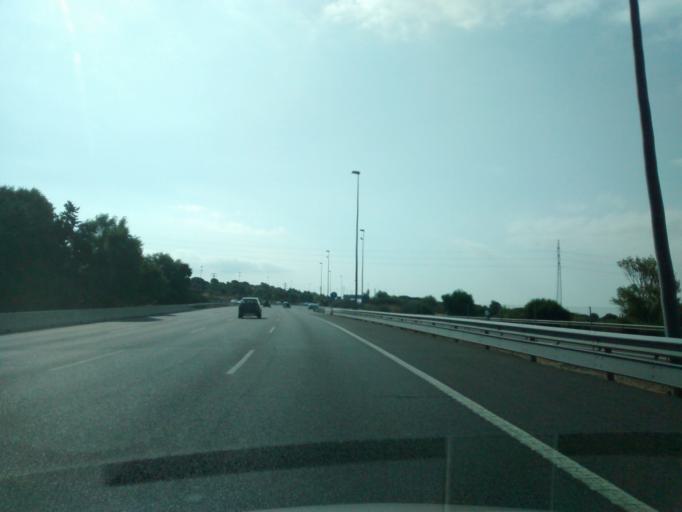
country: ES
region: Madrid
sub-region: Provincia de Madrid
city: Collado-Villalba
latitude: 40.6115
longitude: -3.9782
